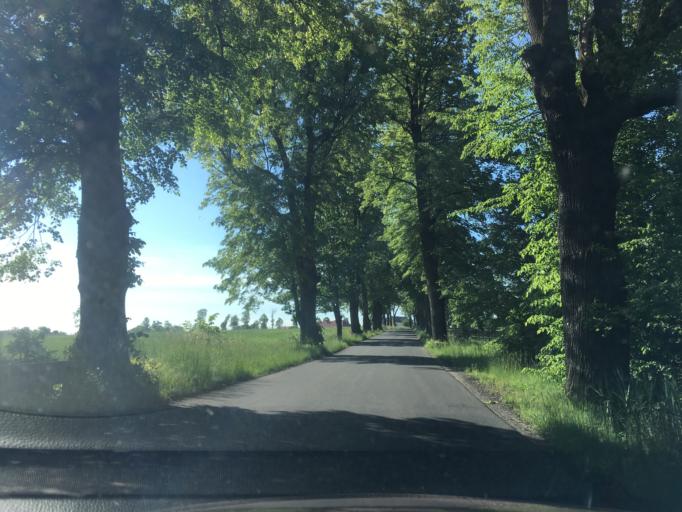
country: PL
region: Lower Silesian Voivodeship
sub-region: Powiat zgorzelecki
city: Sulikow
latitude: 51.1081
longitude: 15.0345
